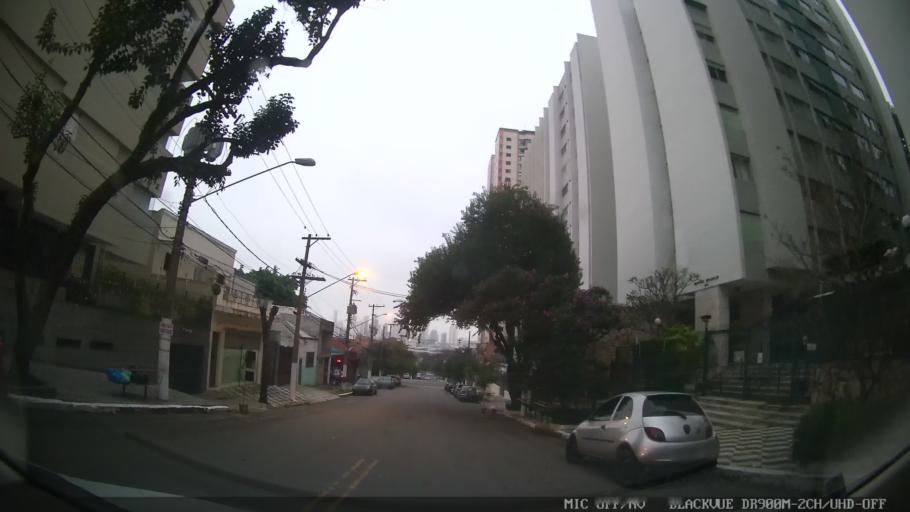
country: BR
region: Sao Paulo
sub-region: Sao Paulo
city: Sao Paulo
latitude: -23.5822
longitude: -46.6066
